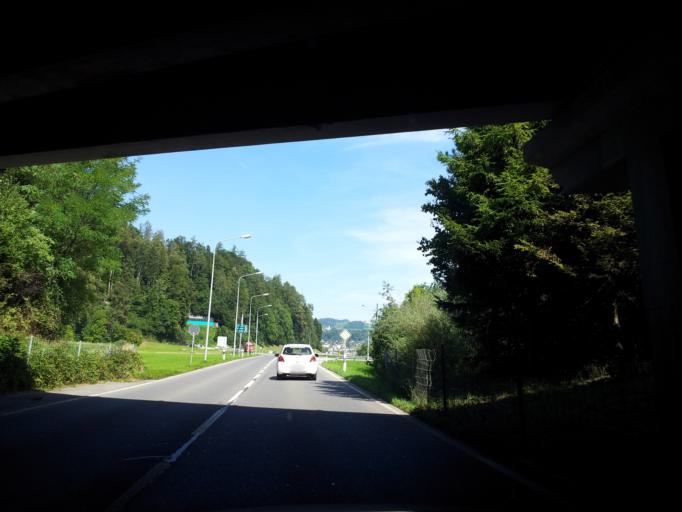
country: CH
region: Schwyz
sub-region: Bezirk March
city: Tuggen
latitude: 47.2103
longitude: 8.9625
